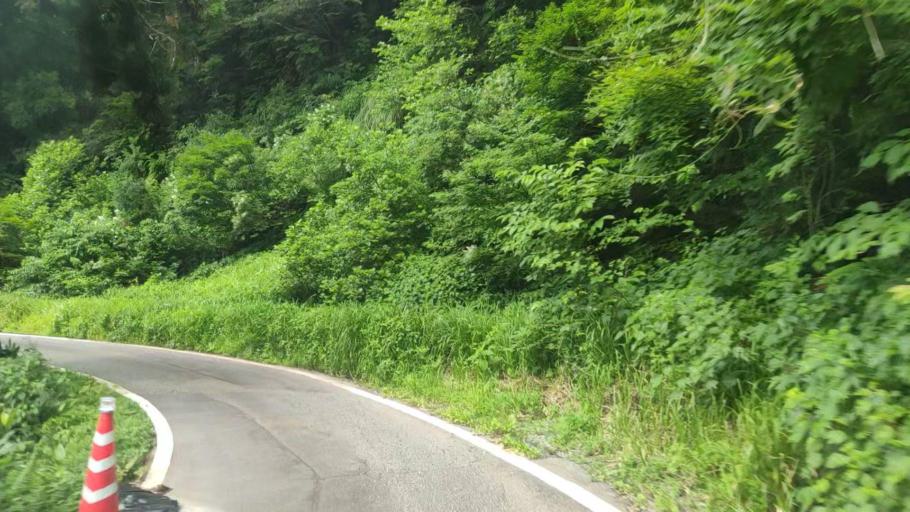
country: JP
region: Fukui
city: Katsuyama
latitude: 36.1790
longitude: 136.5220
